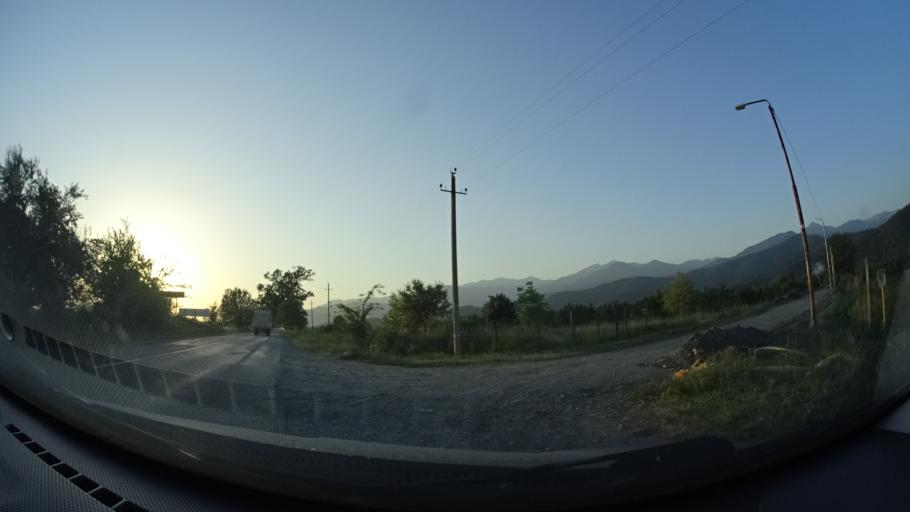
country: GE
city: Bagdadi
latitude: 41.8645
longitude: 46.0172
